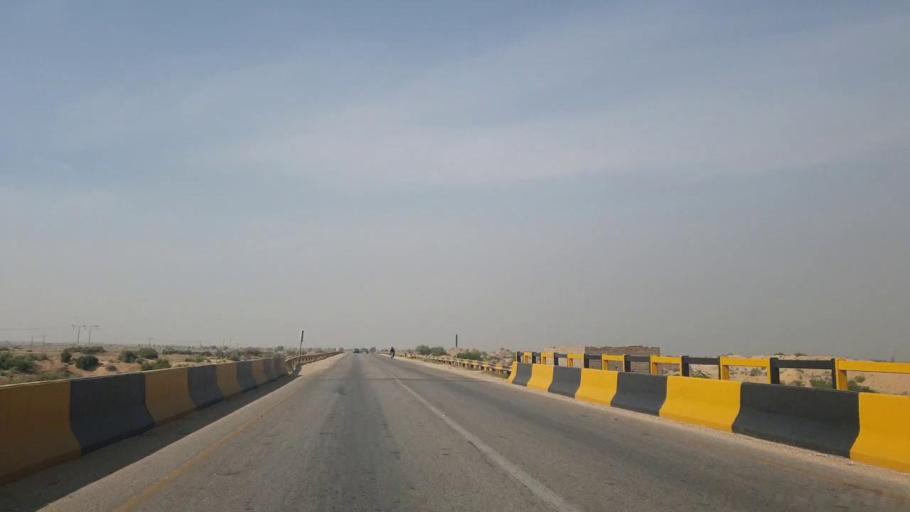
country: PK
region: Sindh
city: Sann
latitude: 26.0372
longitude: 68.1162
